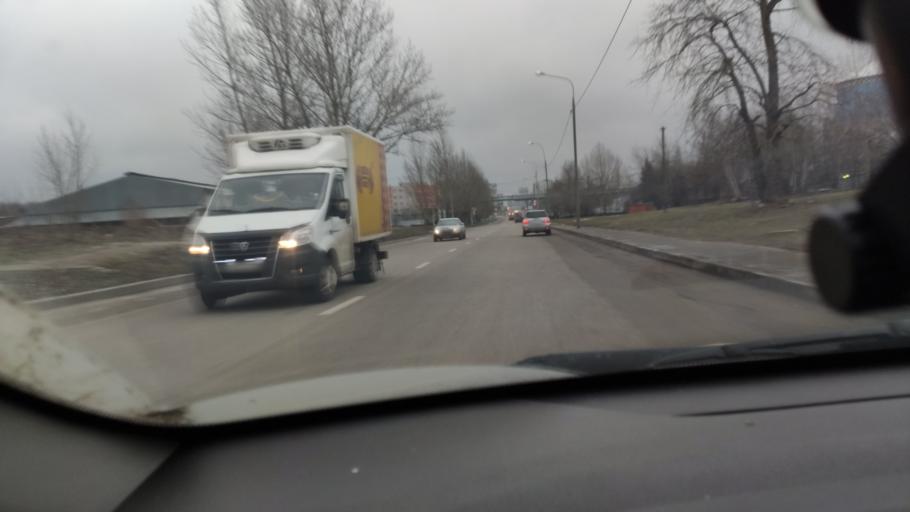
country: RU
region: Moskovskaya
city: Biryulevo Zapadnoye
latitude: 55.5813
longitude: 37.6304
